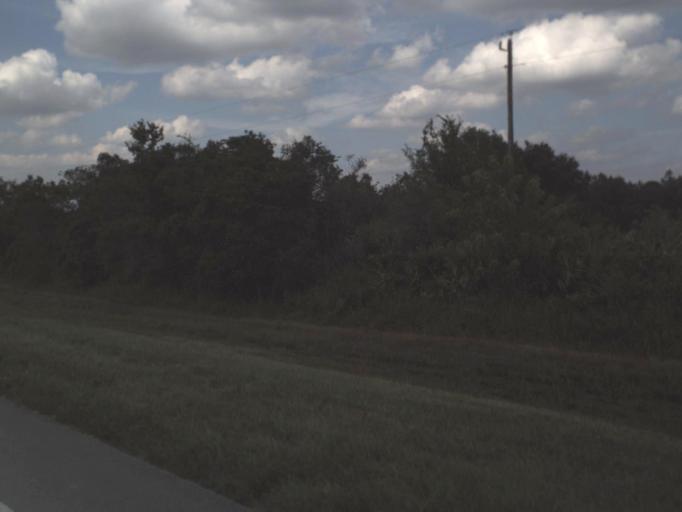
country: US
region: Florida
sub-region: Indian River County
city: Fellsmere
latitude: 27.6260
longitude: -80.8645
